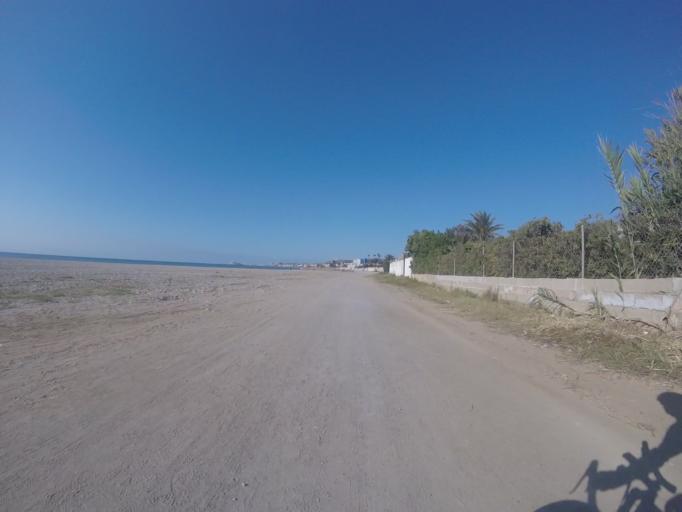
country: ES
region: Valencia
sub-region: Provincia de Castello
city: Benicarlo
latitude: 40.4074
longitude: 0.4244
